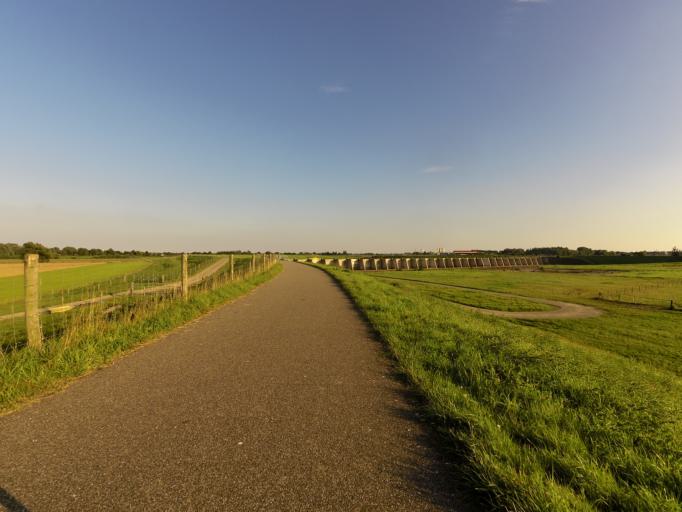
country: NL
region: Gelderland
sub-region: Gemeente Westervoort
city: Westervoort
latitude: 51.9538
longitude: 5.9555
